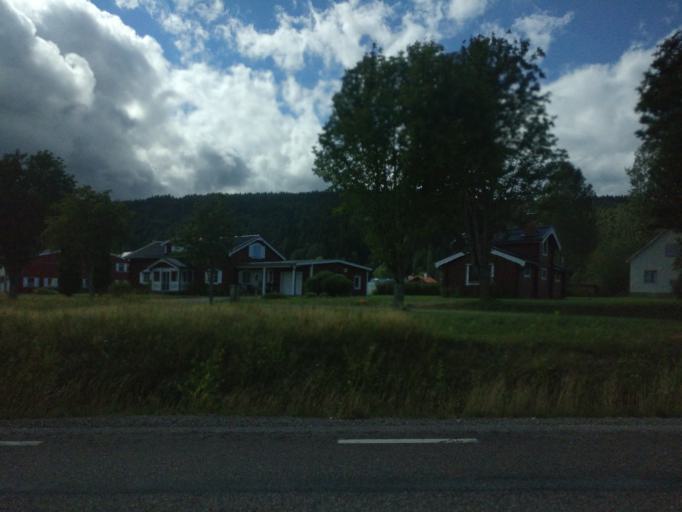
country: SE
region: Vaermland
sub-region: Hagfors Kommun
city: Ekshaerad
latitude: 60.2876
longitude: 13.3971
